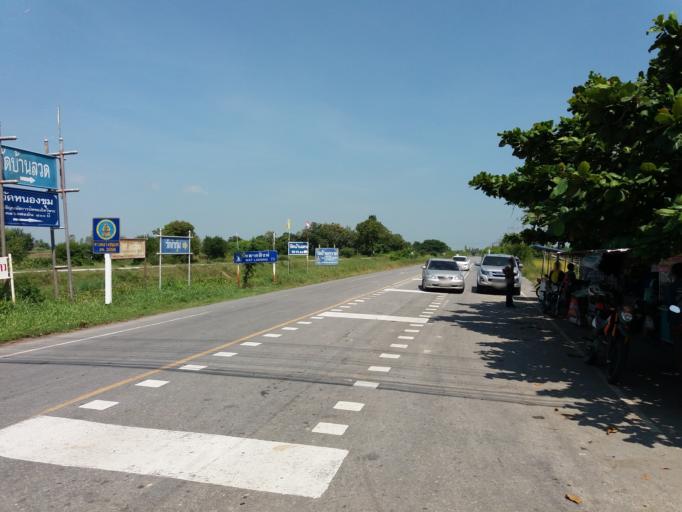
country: TH
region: Suphan Buri
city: Don Chedi
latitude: 14.6268
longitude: 100.0364
